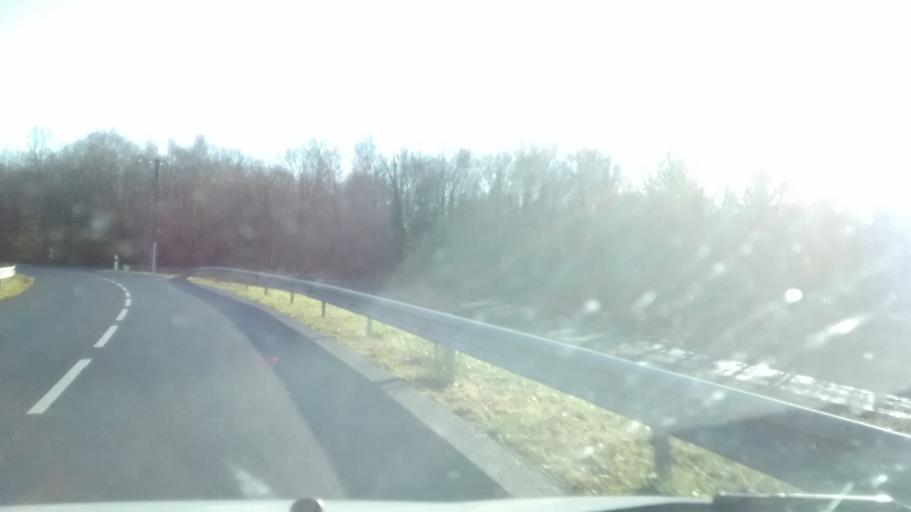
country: FR
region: Centre
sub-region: Departement d'Indre-et-Loire
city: Monnaie
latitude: 47.4916
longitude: 0.8263
